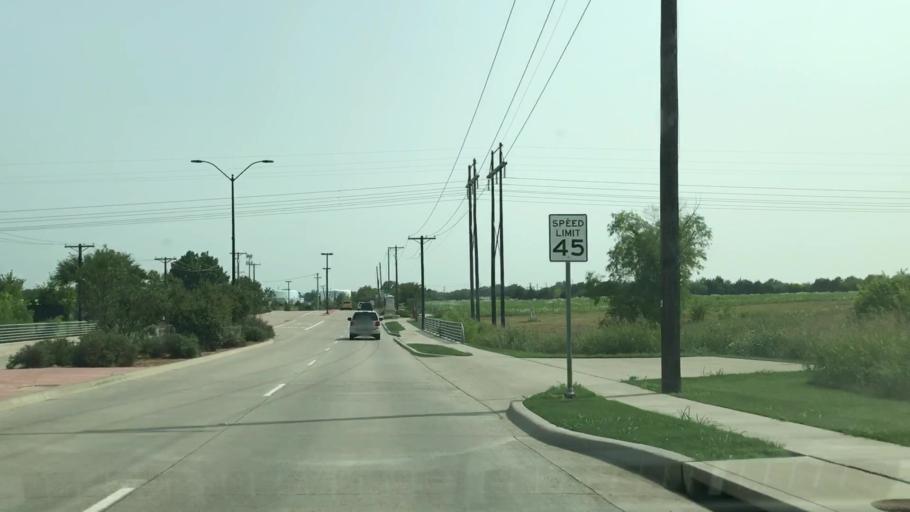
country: US
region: Texas
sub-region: Dallas County
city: Sachse
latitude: 32.9490
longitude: -96.5708
